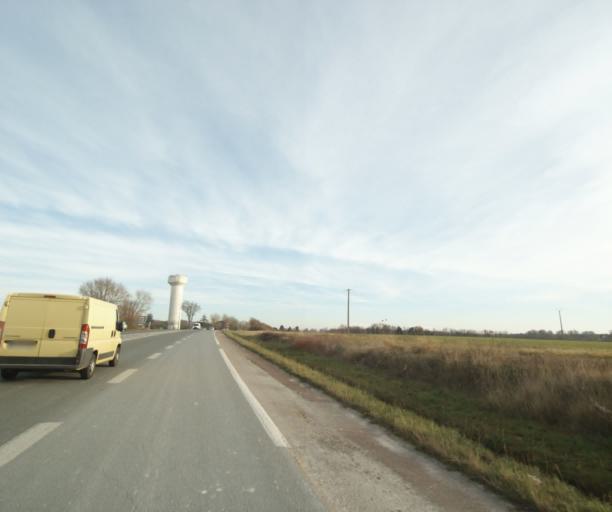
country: FR
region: Poitou-Charentes
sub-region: Departement de la Charente-Maritime
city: Saint-Porchaire
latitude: 45.8107
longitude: -0.7647
